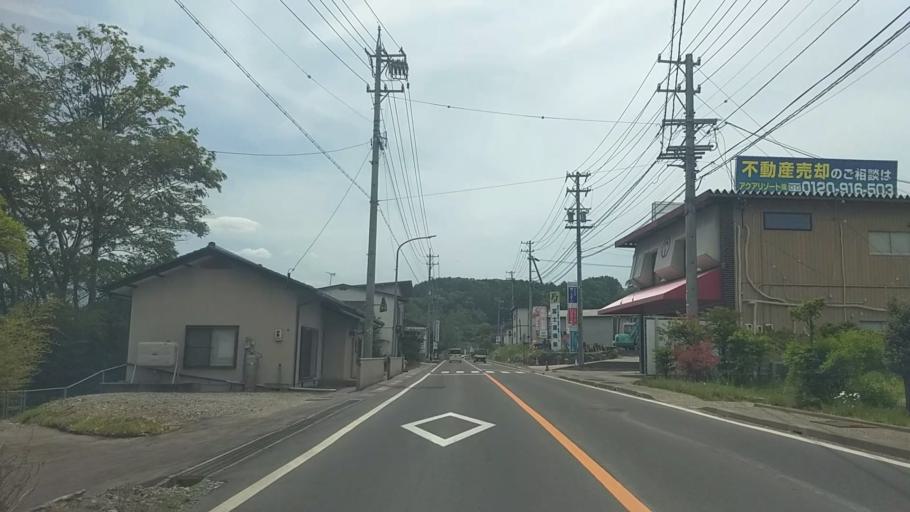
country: JP
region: Nagano
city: Saku
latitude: 36.1819
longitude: 138.4817
